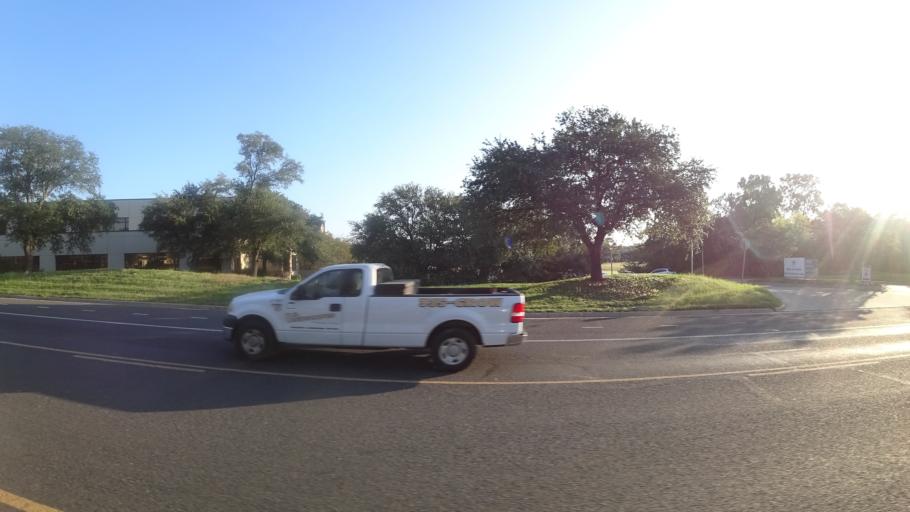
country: US
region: Texas
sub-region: Travis County
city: Austin
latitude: 30.3363
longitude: -97.6814
